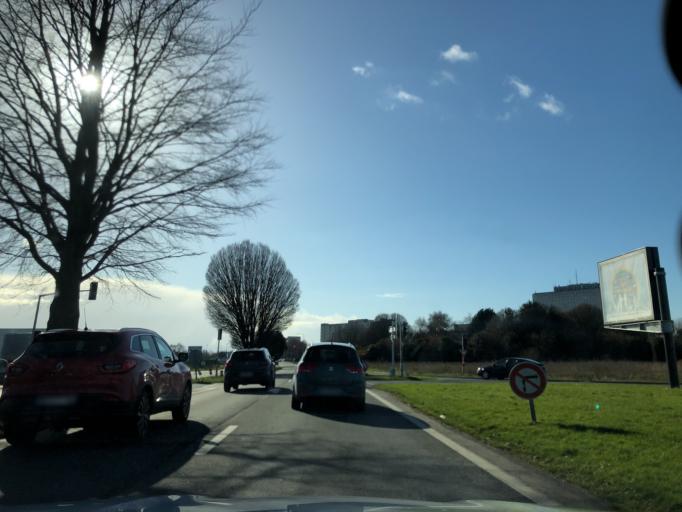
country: FR
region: Lower Normandy
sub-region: Departement du Calvados
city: Caen
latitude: 49.2074
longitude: -0.3484
